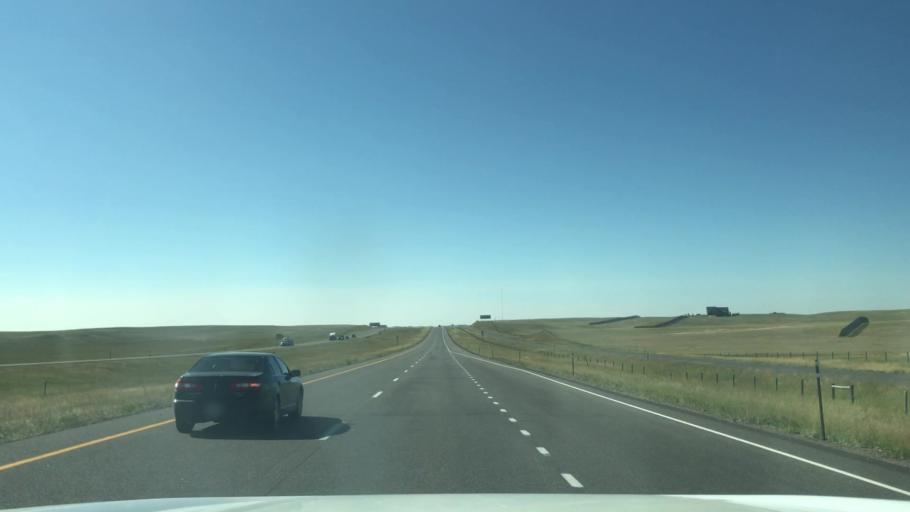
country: US
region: Wyoming
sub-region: Laramie County
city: Ranchettes
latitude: 41.2857
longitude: -104.8495
